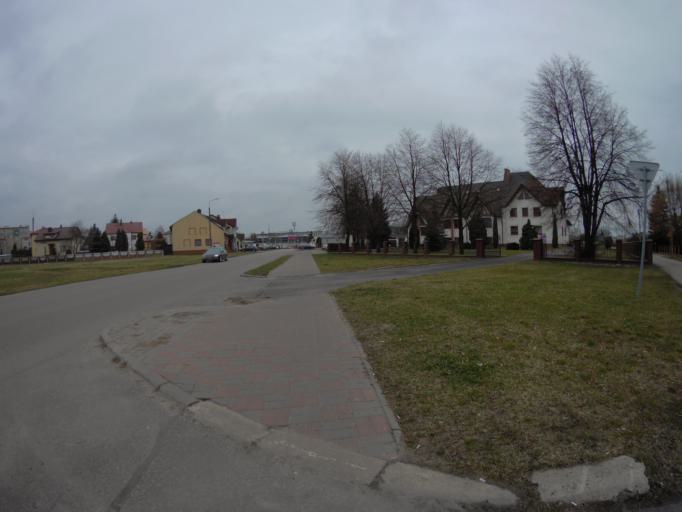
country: PL
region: Lublin Voivodeship
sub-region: Powiat bialski
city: Terespol
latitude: 52.0745
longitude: 23.6053
